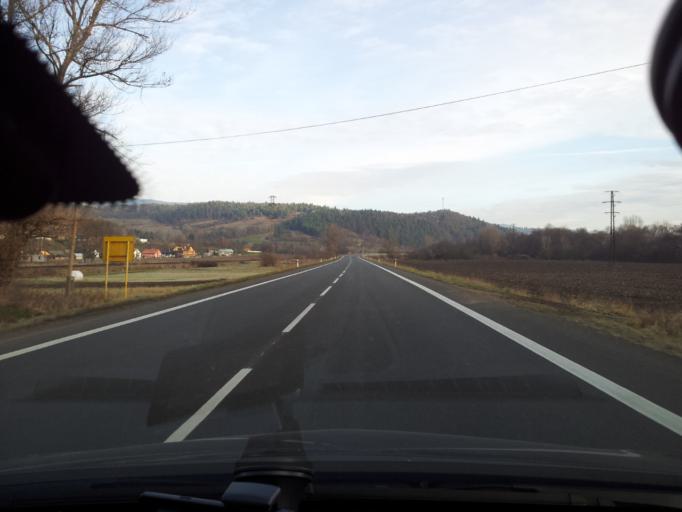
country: SK
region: Banskobystricky
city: Hrochot,Slovakia
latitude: 48.7657
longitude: 19.2828
